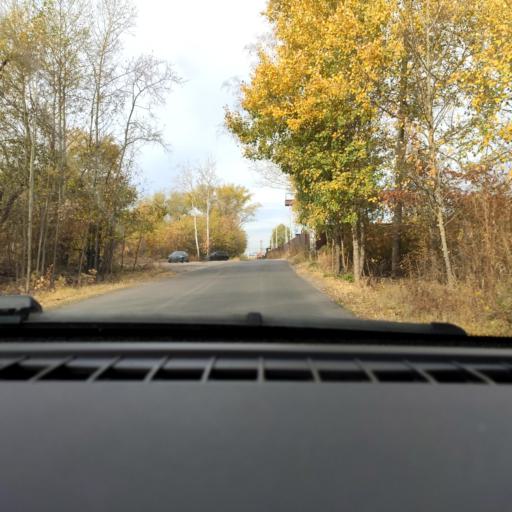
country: RU
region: Voronezj
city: Maslovka
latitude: 51.6403
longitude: 39.2978
